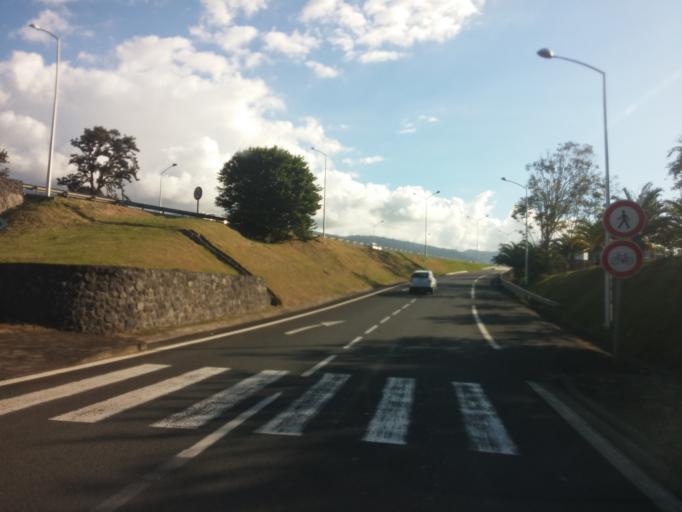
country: RE
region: Reunion
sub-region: Reunion
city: Sainte-Marie
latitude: -20.8967
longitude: 55.5100
